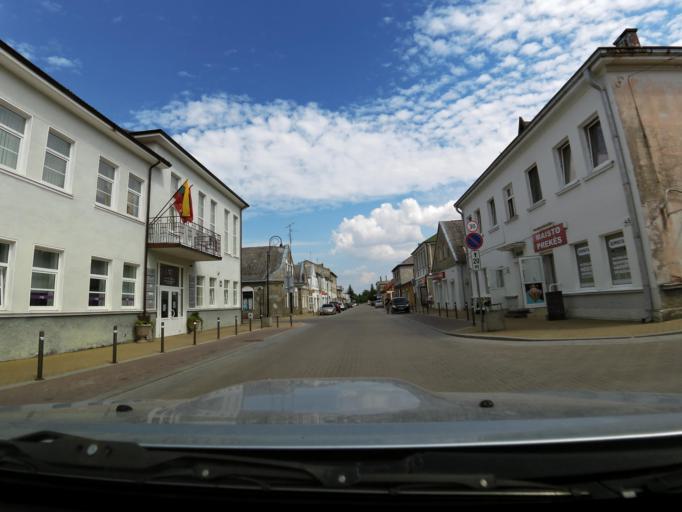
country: LT
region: Taurages apskritis
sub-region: Jurbarkas
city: Jurbarkas
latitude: 55.0761
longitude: 22.7678
